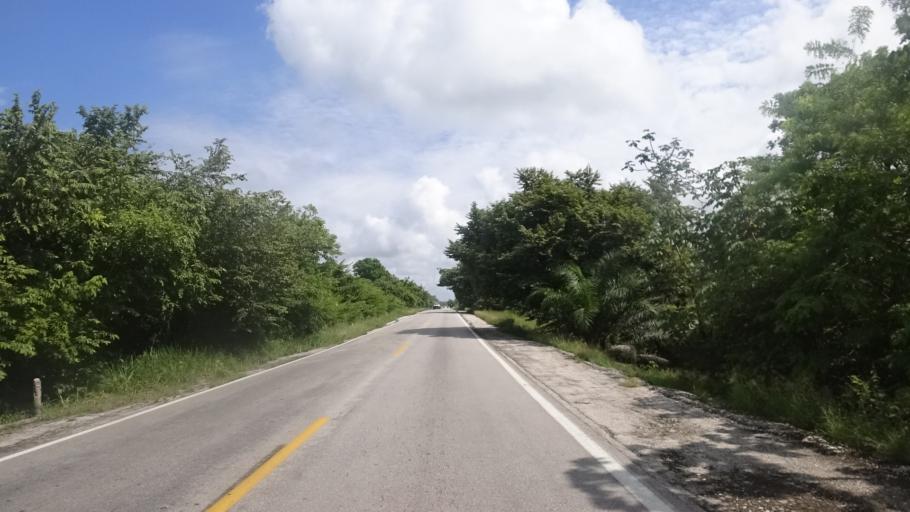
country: MX
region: Chiapas
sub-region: Catazaja
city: Catazaja
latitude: 17.6806
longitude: -92.0261
